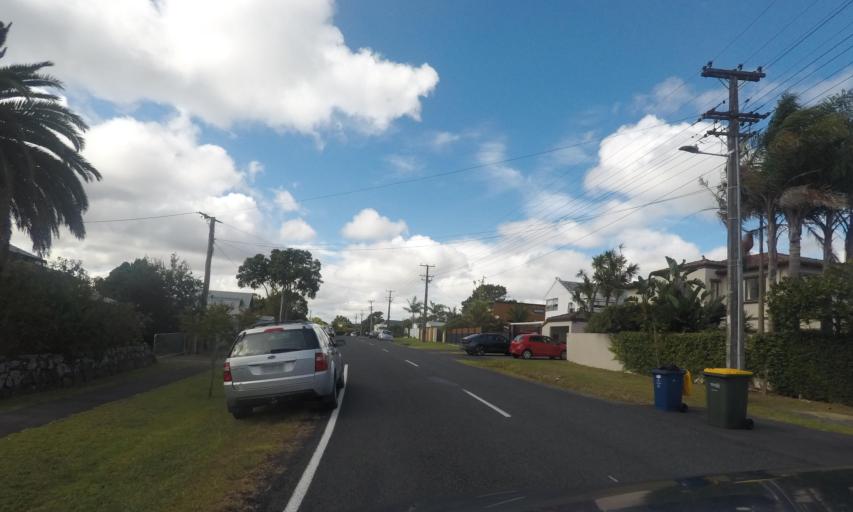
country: NZ
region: Auckland
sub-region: Auckland
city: North Shore
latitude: -36.7797
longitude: 174.6592
